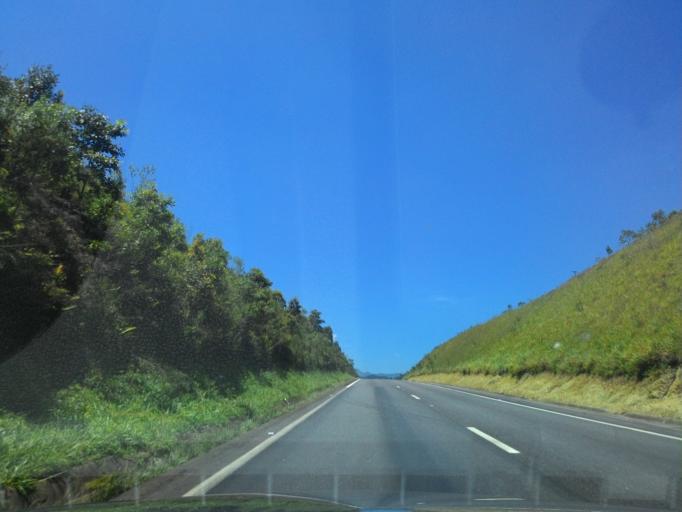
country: BR
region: Parana
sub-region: Antonina
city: Antonina
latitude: -25.0977
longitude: -48.6645
